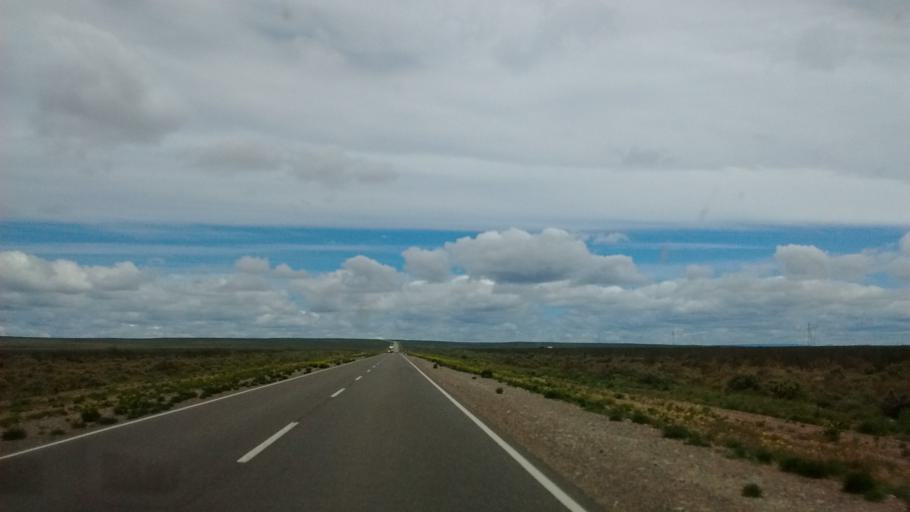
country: AR
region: Neuquen
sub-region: Departamento de Picun Leufu
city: Picun Leufu
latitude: -39.7140
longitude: -69.5213
